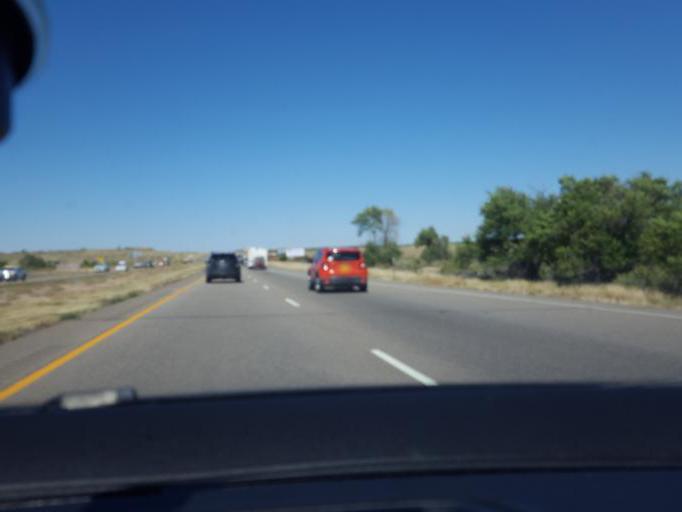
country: US
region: Colorado
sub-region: Pueblo County
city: Pueblo West
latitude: 38.4050
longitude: -104.6155
